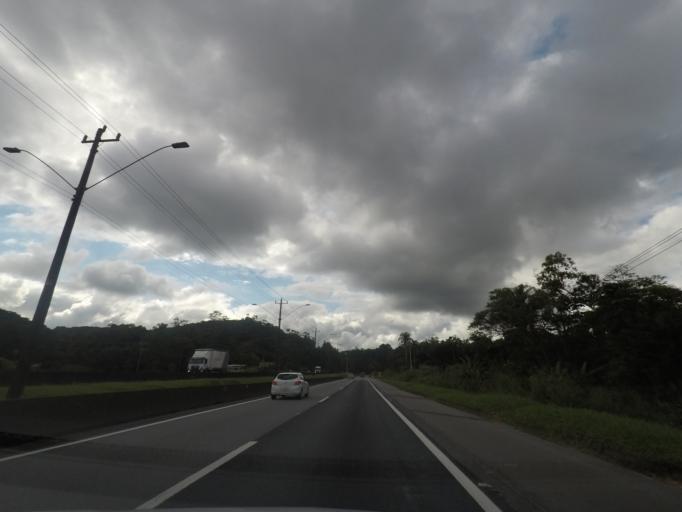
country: BR
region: Sao Paulo
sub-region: Sao Lourenco Da Serra
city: Sao Lourenco da Serra
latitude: -23.9085
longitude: -46.9915
